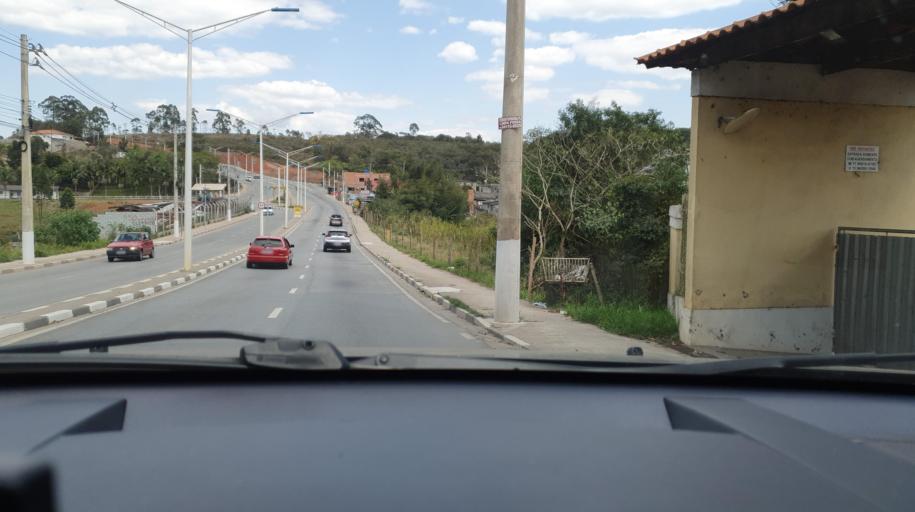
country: BR
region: Sao Paulo
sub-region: Vargem Grande Paulista
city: Vargem Grande Paulista
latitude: -23.6601
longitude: -47.0061
